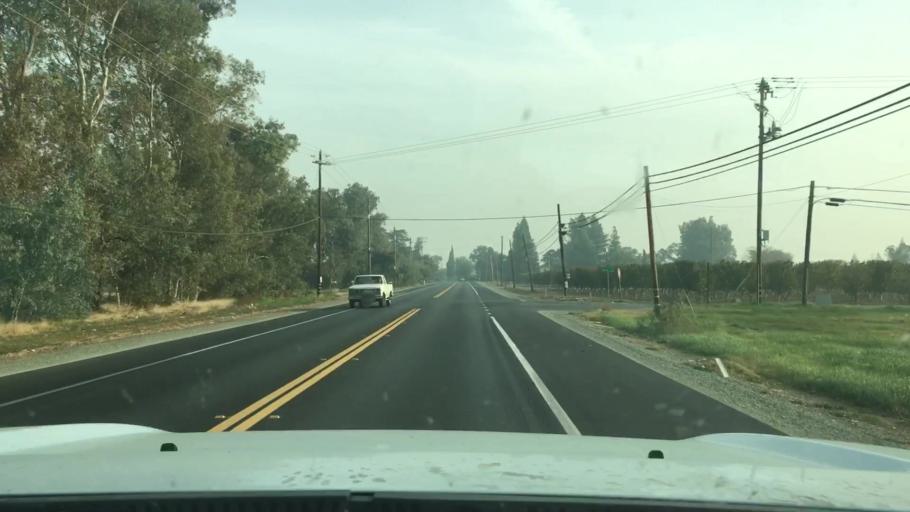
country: US
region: California
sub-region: San Joaquin County
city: Garden Acres
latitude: 38.0006
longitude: -121.2254
